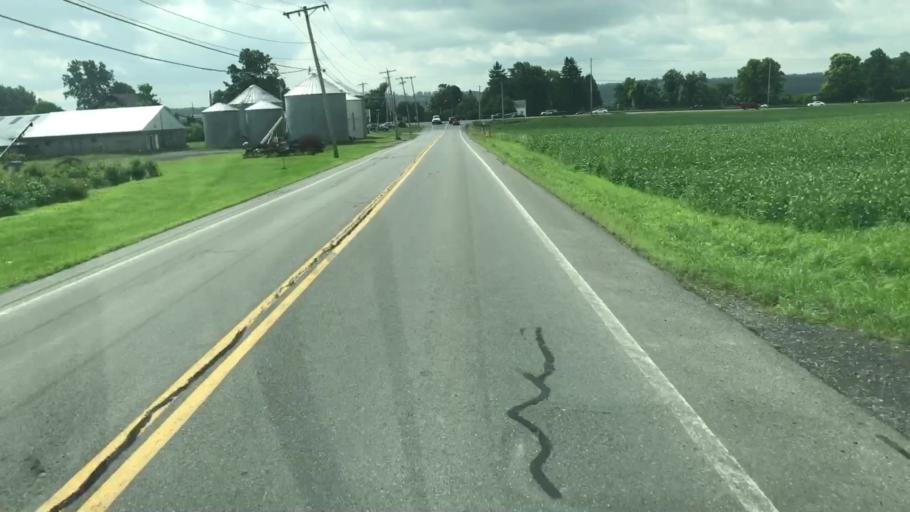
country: US
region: New York
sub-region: Onondaga County
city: Marcellus
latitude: 43.0370
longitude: -76.3655
